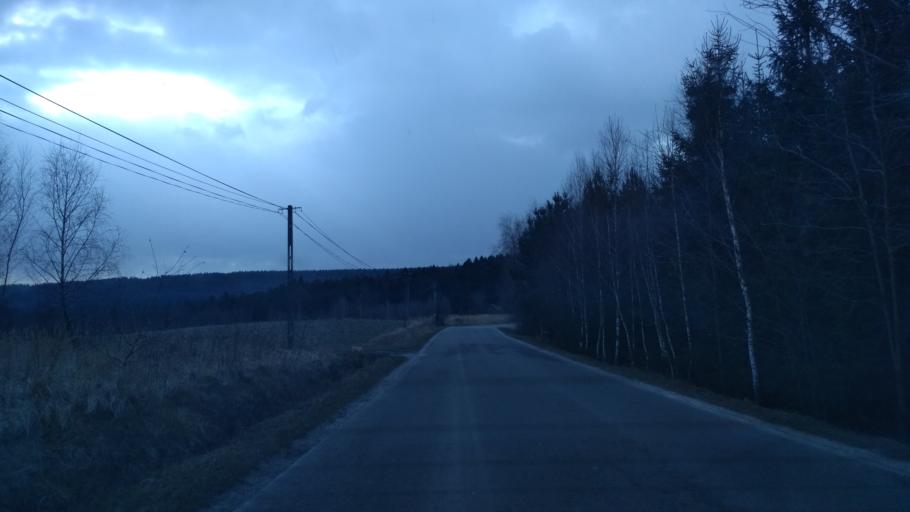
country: PL
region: Subcarpathian Voivodeship
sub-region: Powiat rzeszowski
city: Blazowa
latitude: 49.8628
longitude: 22.0976
